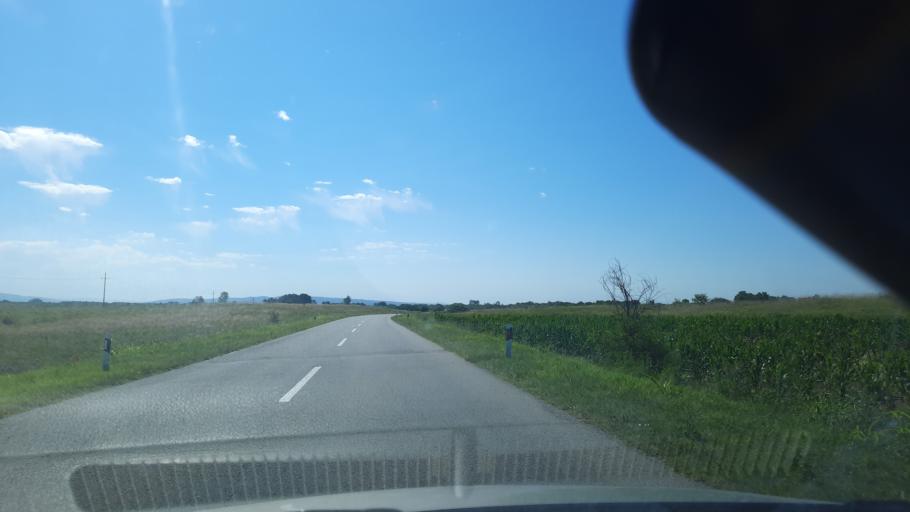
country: RS
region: Central Serbia
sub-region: Branicevski Okrug
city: Pozarevac
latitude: 44.8059
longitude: 21.1745
